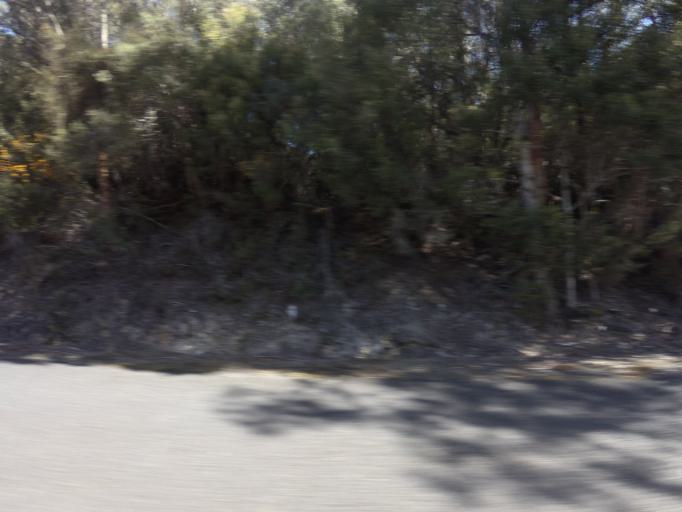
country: AU
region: Tasmania
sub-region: Derwent Valley
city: New Norfolk
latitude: -42.7667
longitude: 146.5573
